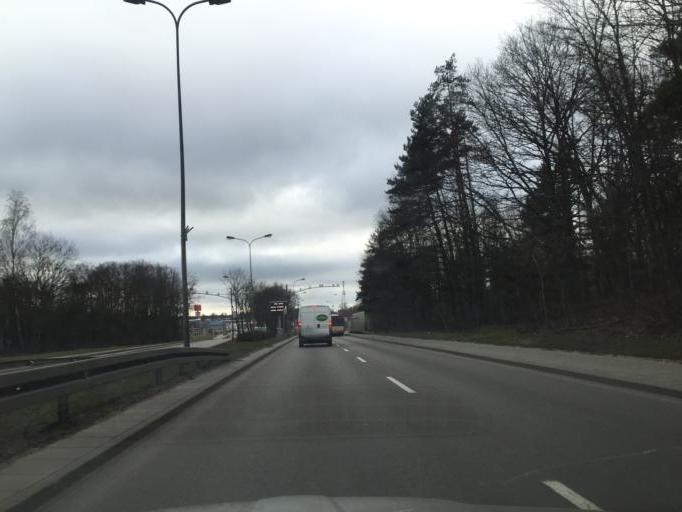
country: PL
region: Pomeranian Voivodeship
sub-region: Sopot
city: Sopot
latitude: 54.3765
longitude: 18.5284
